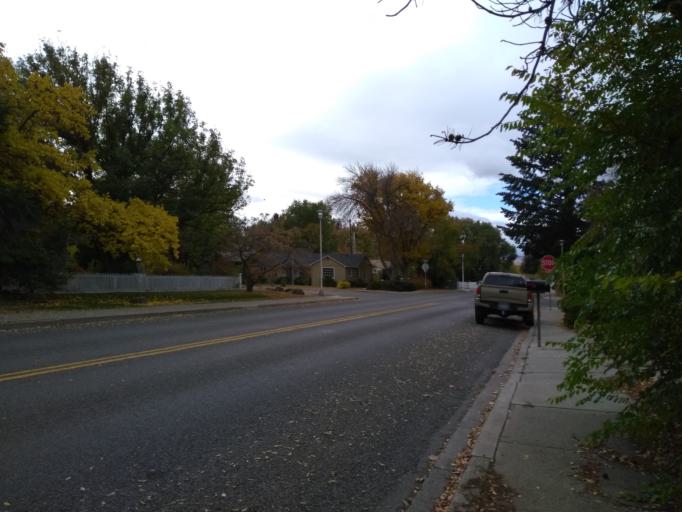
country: US
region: Washington
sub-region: Kittitas County
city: Ellensburg
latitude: 46.9883
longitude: -120.5450
